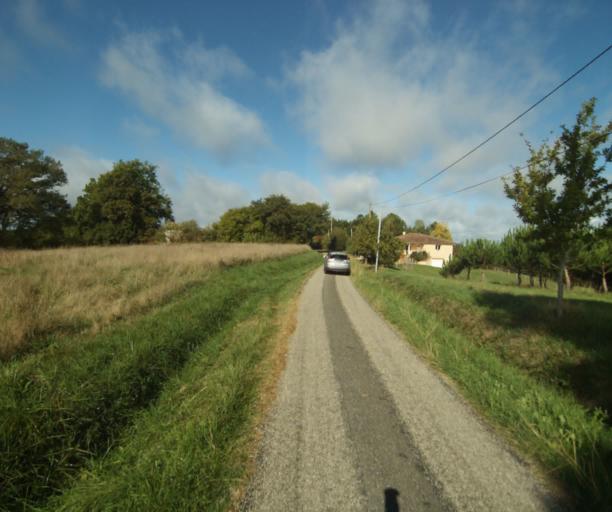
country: FR
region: Midi-Pyrenees
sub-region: Departement du Gers
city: Cazaubon
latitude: 43.8472
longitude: -0.0642
